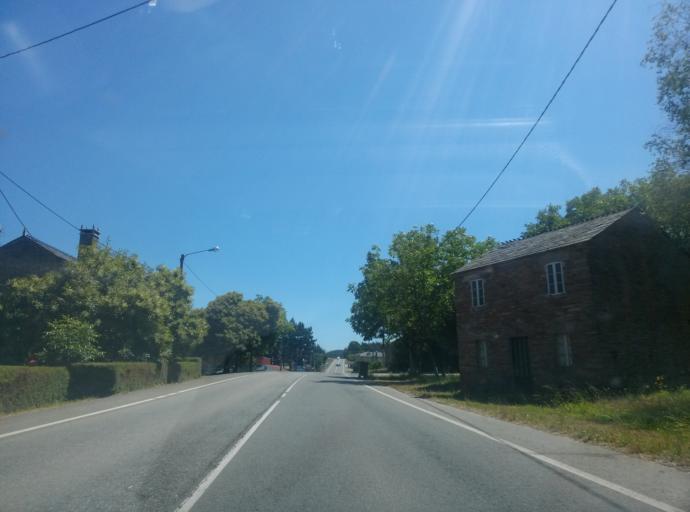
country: ES
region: Galicia
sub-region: Provincia de Lugo
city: Castro de Rei
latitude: 43.2454
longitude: -7.4127
